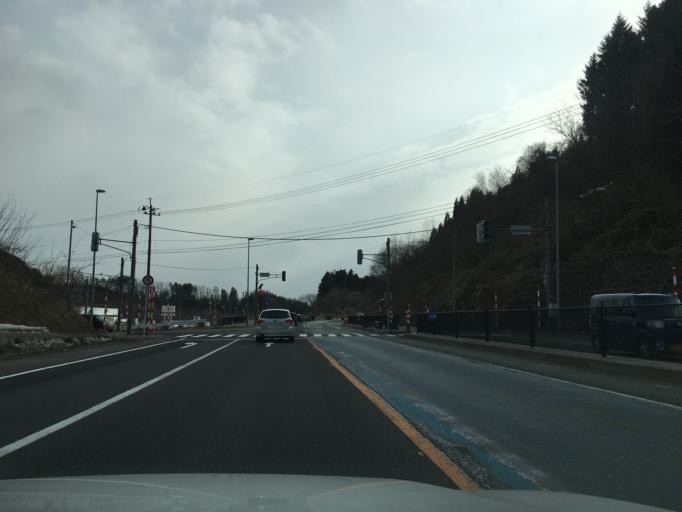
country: JP
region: Aomori
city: Namioka
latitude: 40.7741
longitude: 140.5994
